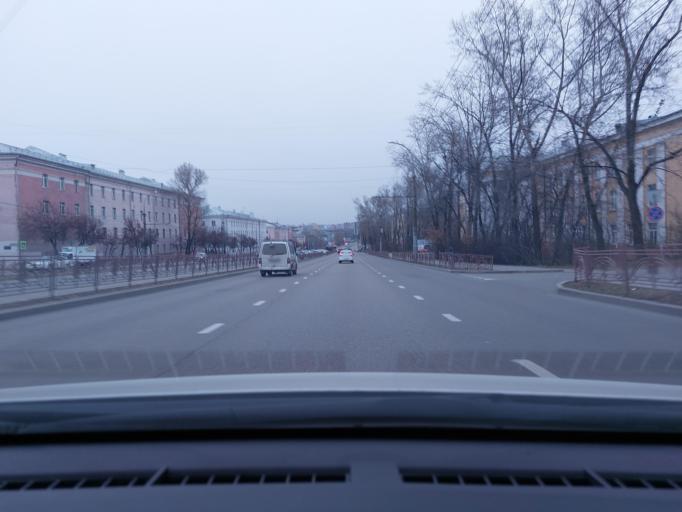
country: RU
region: Irkutsk
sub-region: Irkutskiy Rayon
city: Irkutsk
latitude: 52.2603
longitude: 104.2610
